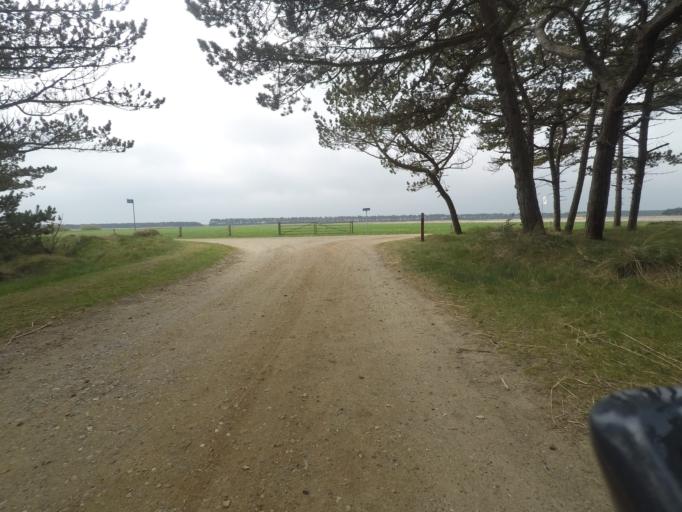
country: DE
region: Schleswig-Holstein
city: List
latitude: 55.0945
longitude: 8.5185
